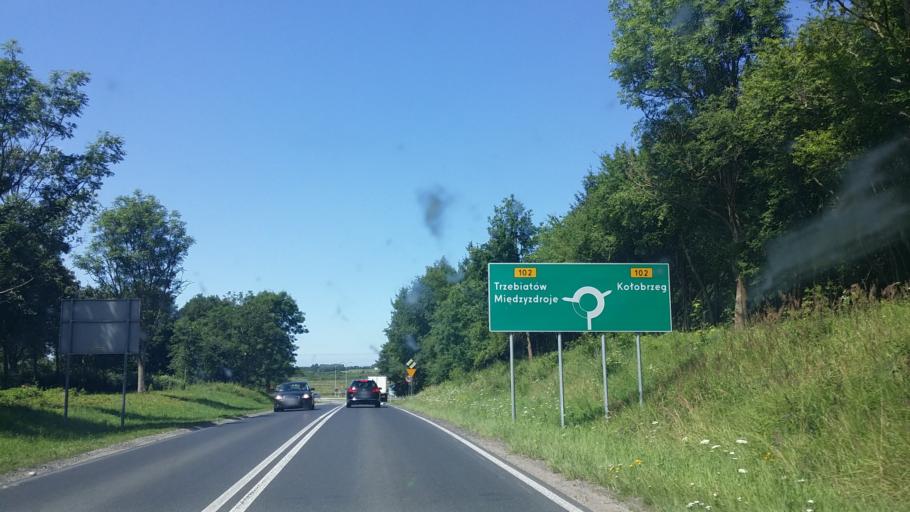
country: PL
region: West Pomeranian Voivodeship
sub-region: Powiat kolobrzeski
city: Kolobrzeg
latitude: 54.1293
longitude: 15.5663
